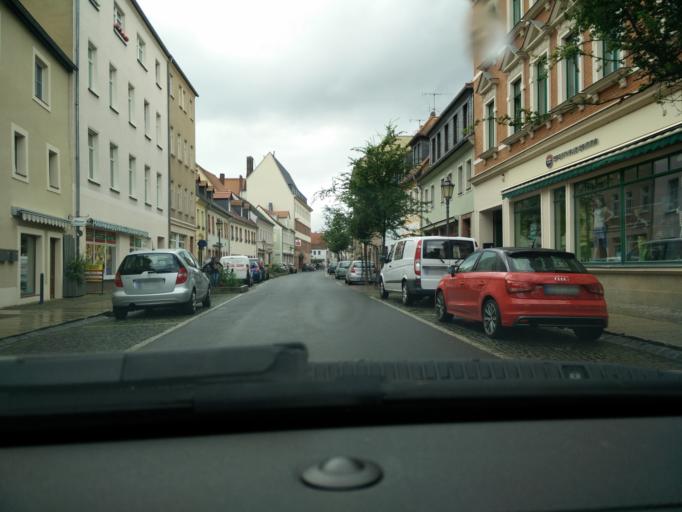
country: DE
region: Saxony
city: Grimma
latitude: 51.2381
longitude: 12.7295
